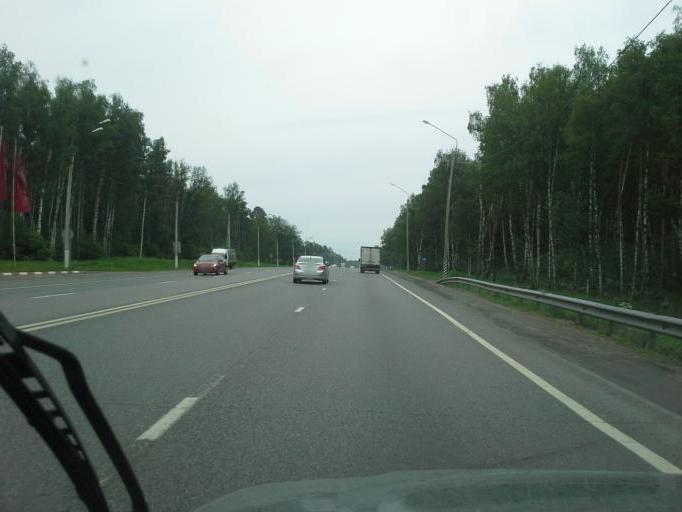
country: RU
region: Vladimir
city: Pokrov
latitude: 55.9018
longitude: 39.0806
